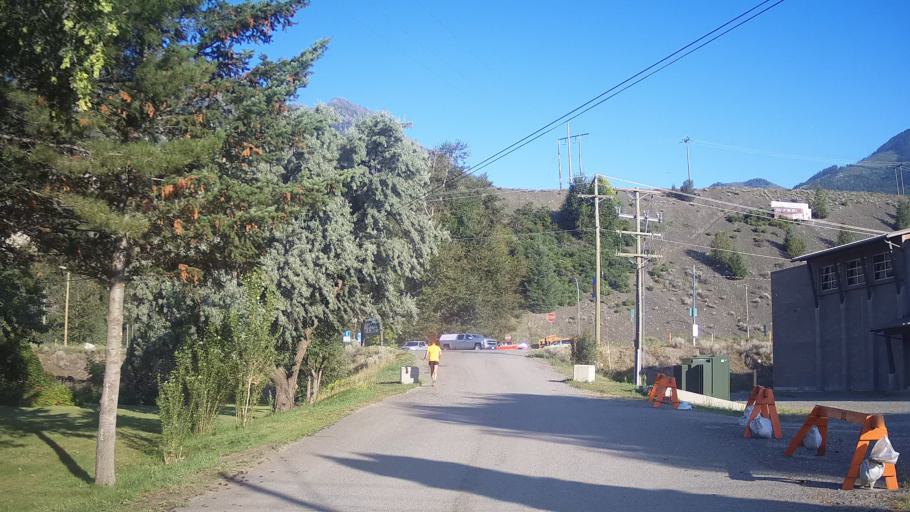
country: CA
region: British Columbia
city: Lillooet
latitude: 50.6803
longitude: -121.9327
